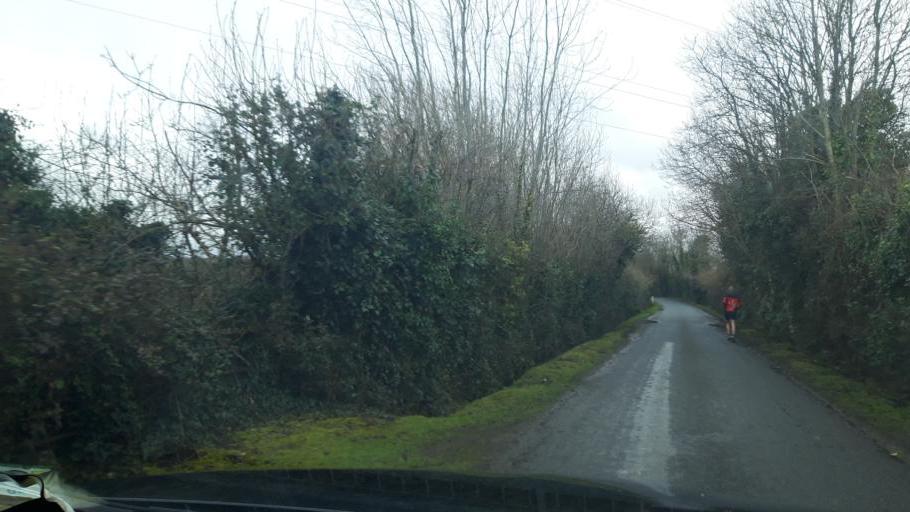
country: IE
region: Leinster
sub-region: South Dublin
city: Newcastle
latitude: 53.3315
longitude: -6.5028
